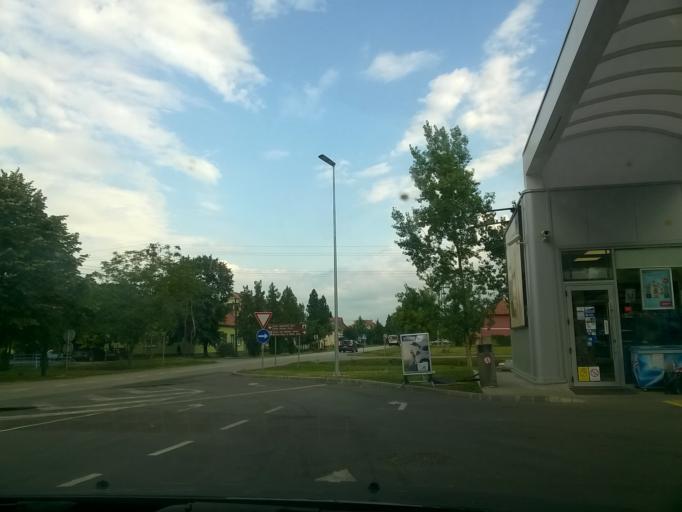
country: RS
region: Autonomna Pokrajina Vojvodina
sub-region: Juznobanatski Okrug
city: Kovacica
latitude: 45.1133
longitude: 20.6183
